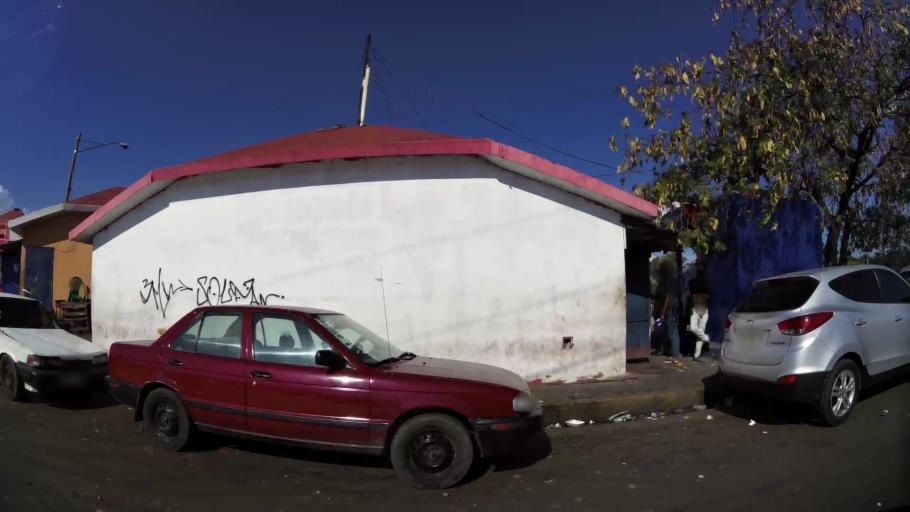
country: DO
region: Nacional
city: Santo Domingo
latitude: 18.4781
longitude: -69.9690
